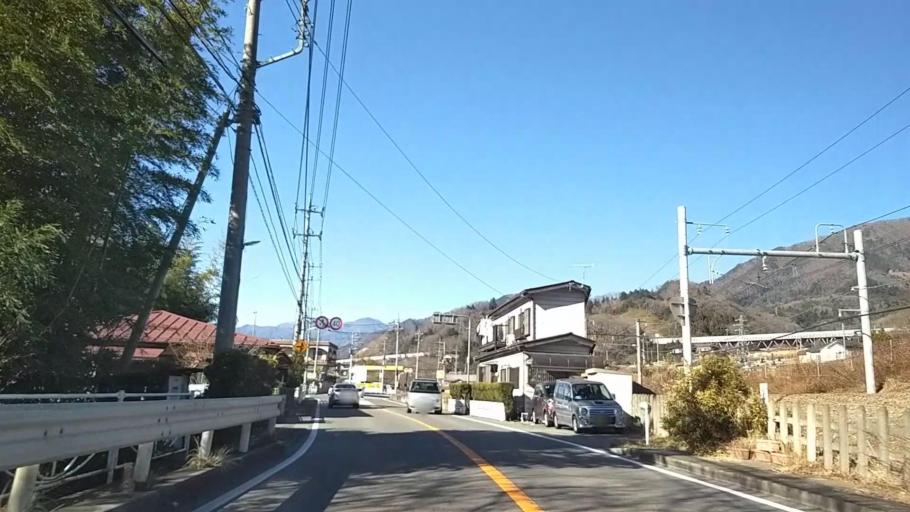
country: JP
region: Yamanashi
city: Otsuki
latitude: 35.6055
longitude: 139.0158
